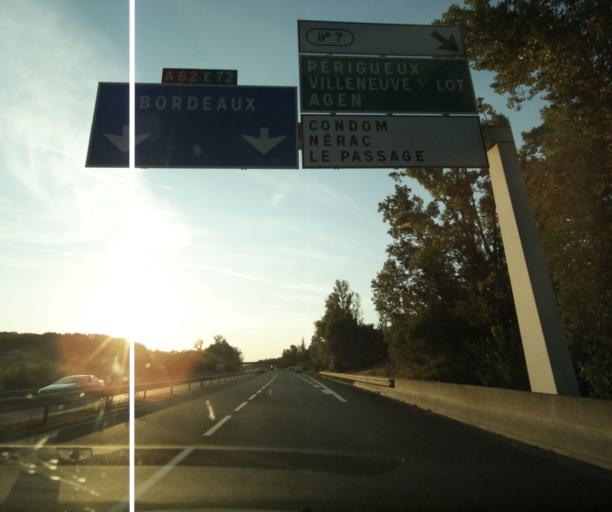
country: FR
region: Aquitaine
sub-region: Departement du Lot-et-Garonne
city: Boe
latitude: 44.1615
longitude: 0.6079
